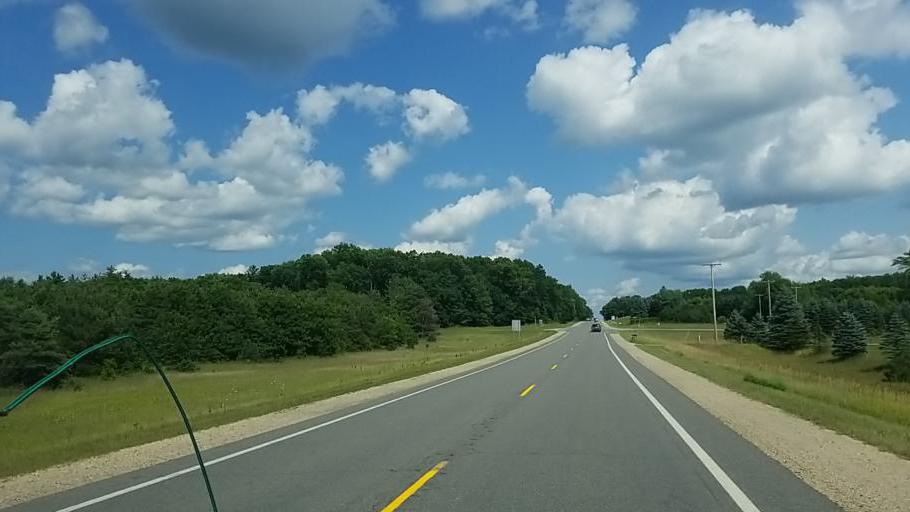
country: US
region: Michigan
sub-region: Montcalm County
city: Howard City
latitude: 43.3958
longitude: -85.6049
